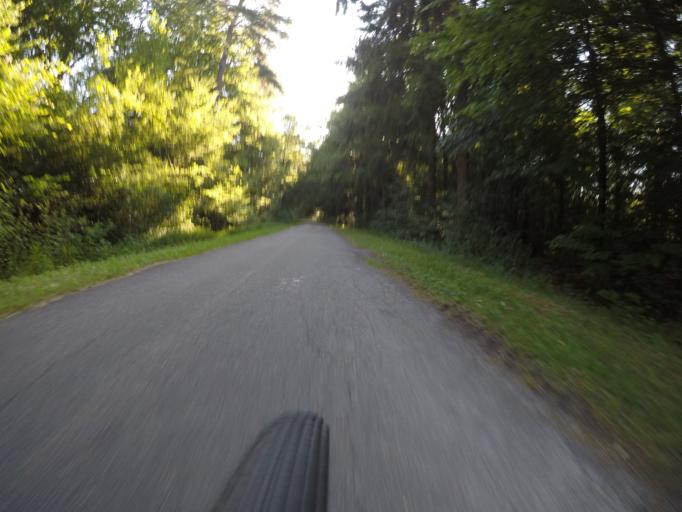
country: DE
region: Baden-Wuerttemberg
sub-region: Regierungsbezirk Stuttgart
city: Sindelfingen
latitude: 48.7215
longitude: 9.0411
